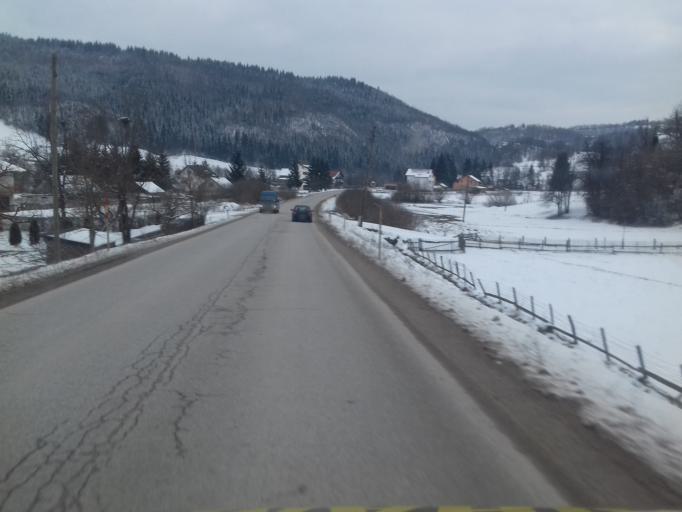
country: BA
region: Republika Srpska
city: Pale
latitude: 43.8713
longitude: 18.5566
